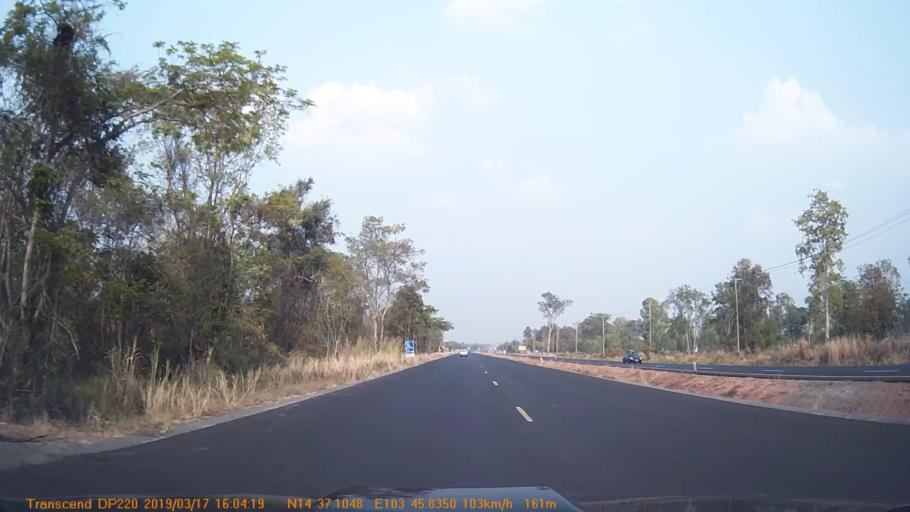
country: TH
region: Surin
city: Sangkha
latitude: 14.6184
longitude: 103.7642
